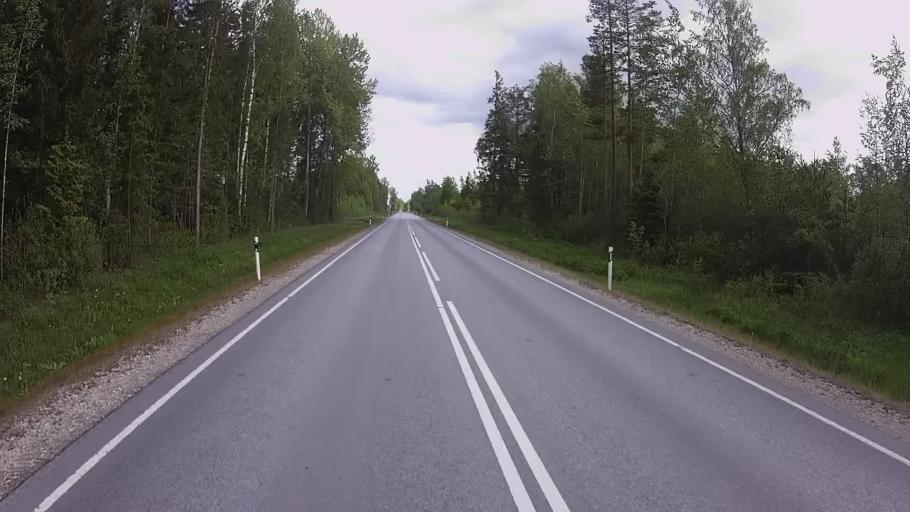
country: EE
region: Jogevamaa
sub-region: Mustvee linn
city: Mustvee
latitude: 58.9724
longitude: 26.8276
